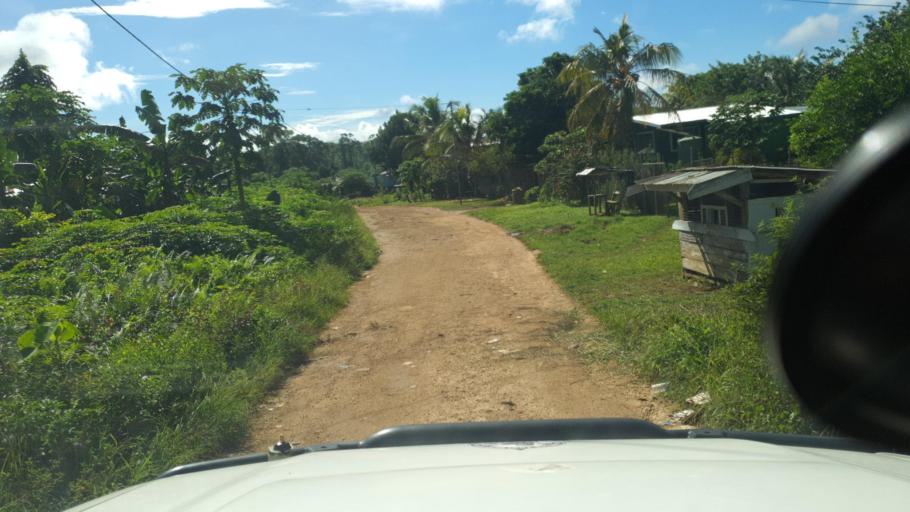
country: SB
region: Western Province
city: Gizo
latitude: -8.2415
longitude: 157.2005
